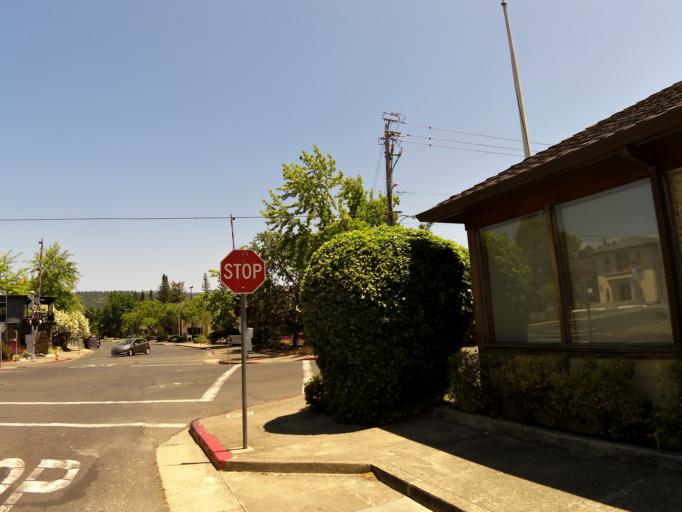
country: US
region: California
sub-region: Napa County
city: Saint Helena
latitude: 38.5058
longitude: -122.4697
